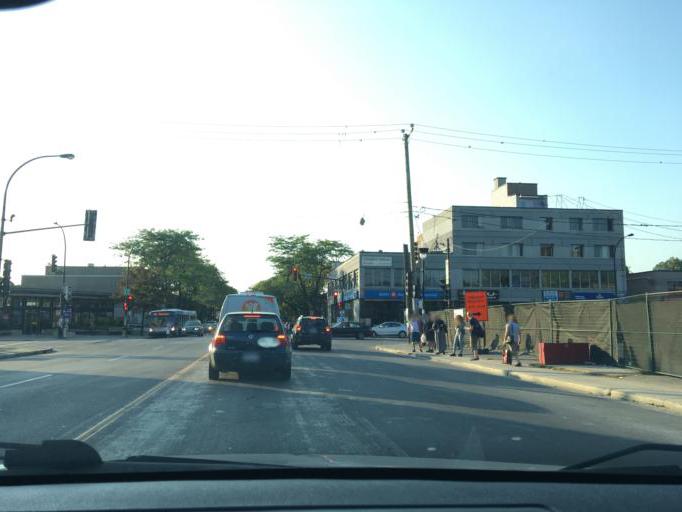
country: CA
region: Quebec
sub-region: Montreal
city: Saint-Leonard
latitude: 45.5477
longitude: -73.6064
